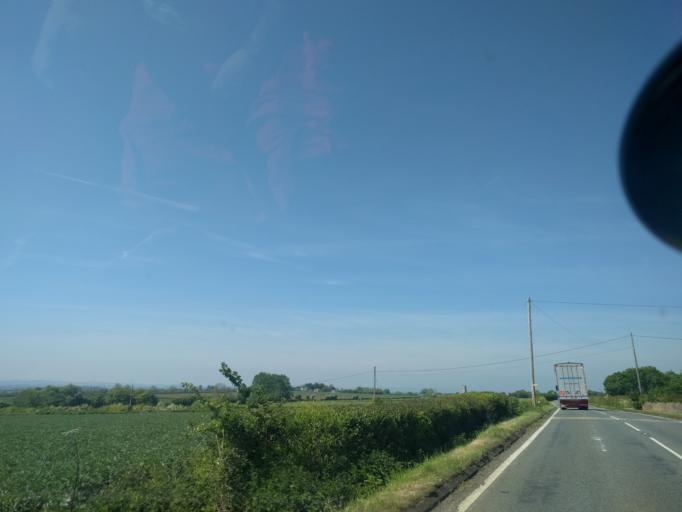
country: GB
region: England
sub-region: Somerset
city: Martock
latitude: 51.0286
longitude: -2.7411
